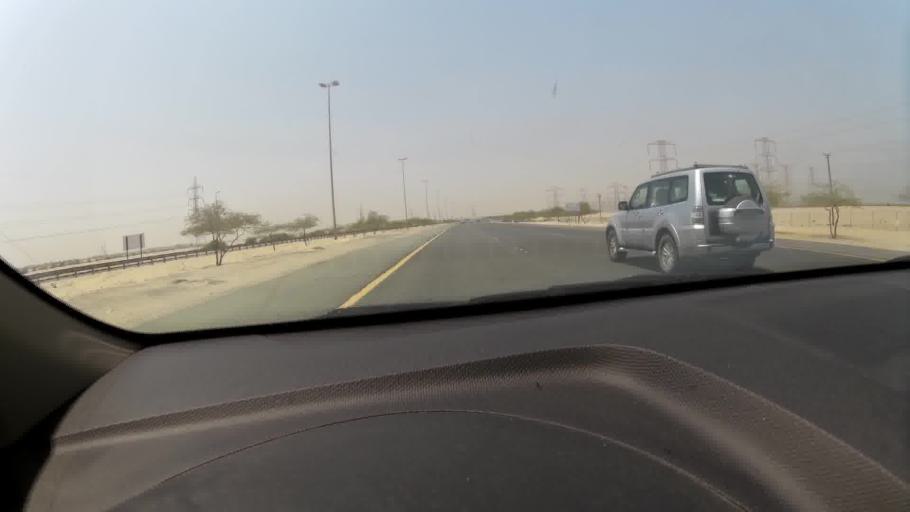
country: KW
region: Al Ahmadi
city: Al Fahahil
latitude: 28.9493
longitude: 48.1339
